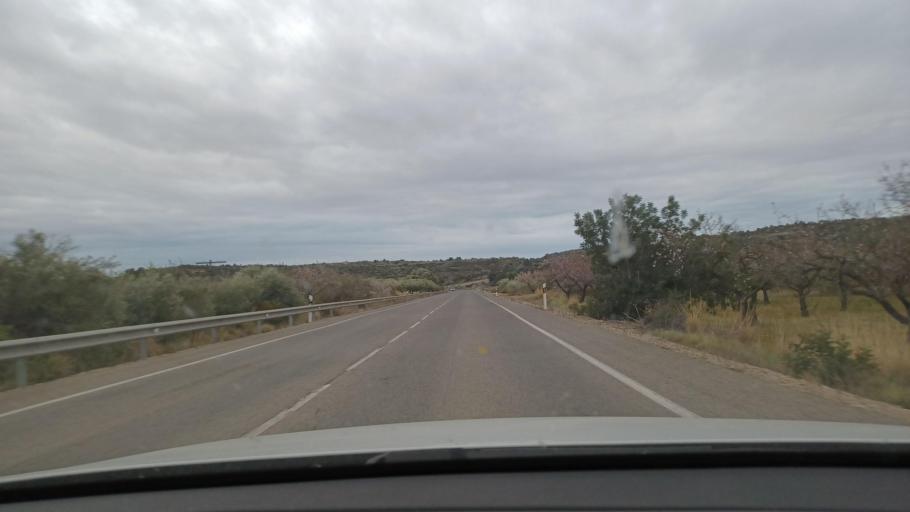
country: ES
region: Valencia
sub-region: Provincia de Castello
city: Traiguera
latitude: 40.5225
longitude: 0.3047
